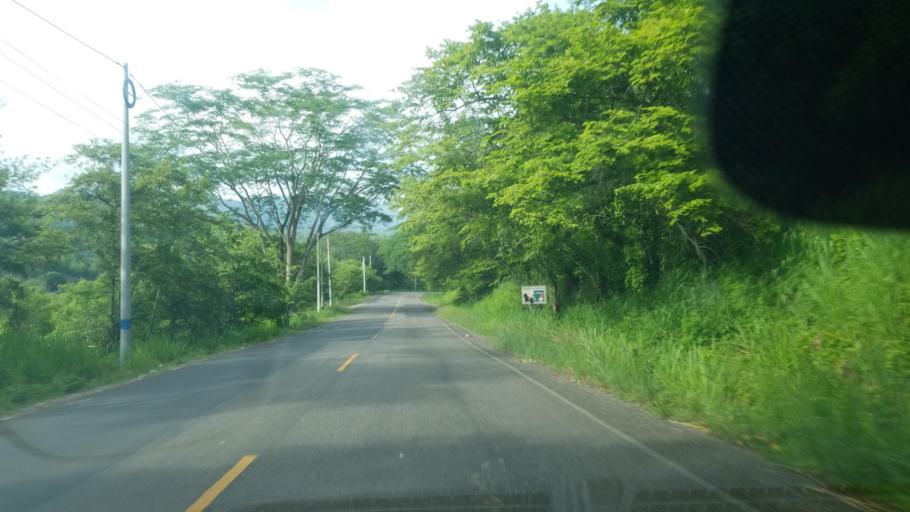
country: HN
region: Santa Barbara
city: Trinidad
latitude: 15.1364
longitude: -88.2452
